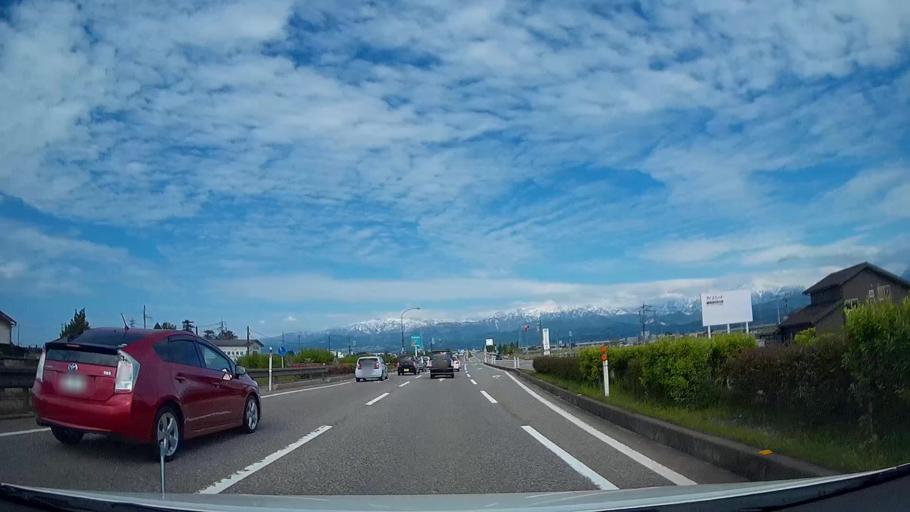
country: JP
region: Toyama
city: Namerikawa
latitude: 36.7185
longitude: 137.2958
